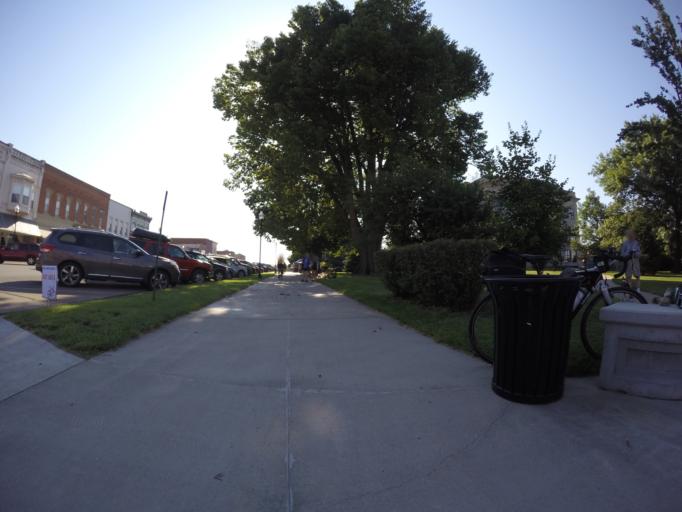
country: US
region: Kansas
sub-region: Brown County
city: Hiawatha
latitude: 39.8528
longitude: -95.5371
